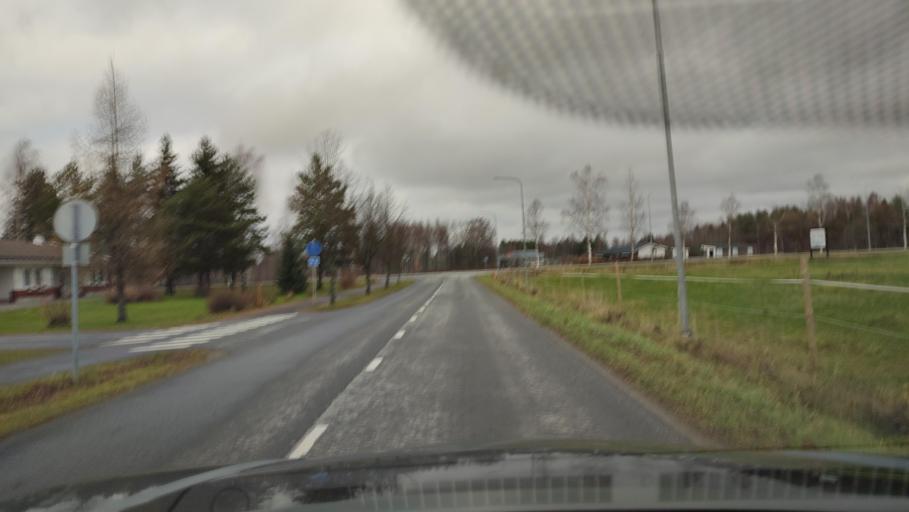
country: FI
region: Southern Ostrobothnia
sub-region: Suupohja
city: Kauhajoki
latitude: 62.4166
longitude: 22.1851
